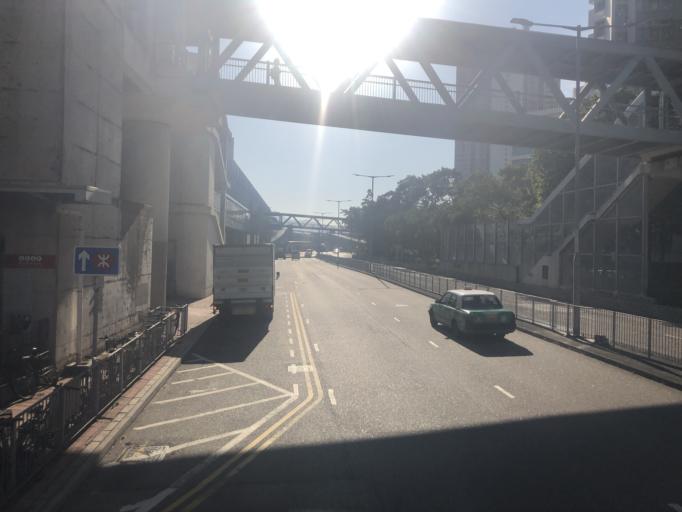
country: HK
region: Yuen Long
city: Yuen Long Kau Hui
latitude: 22.4494
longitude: 114.0054
